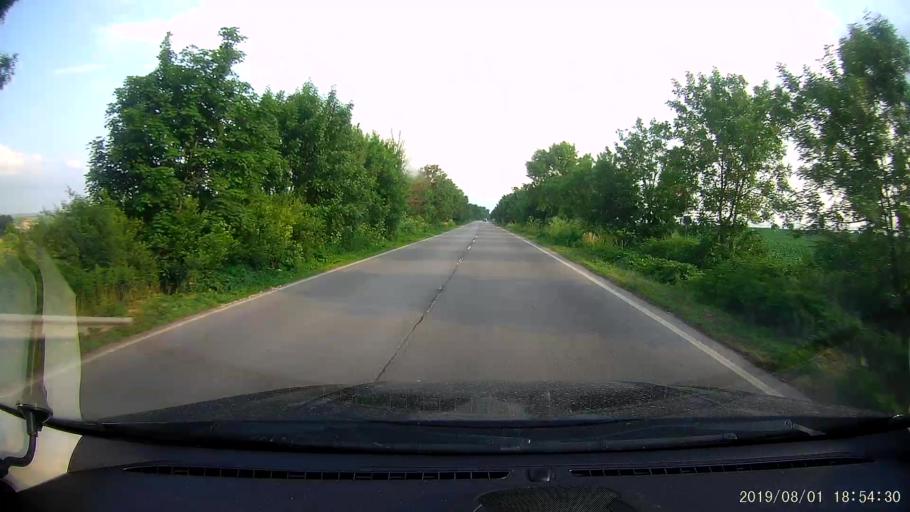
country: BG
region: Shumen
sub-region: Obshtina Shumen
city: Shumen
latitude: 43.1972
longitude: 27.0020
